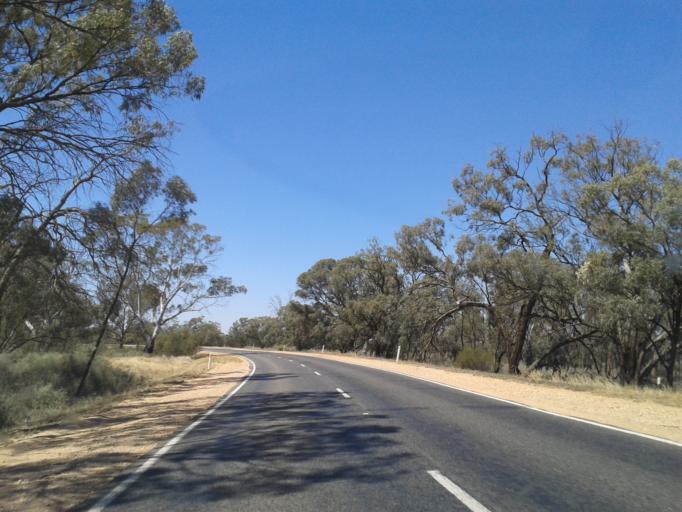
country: AU
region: Victoria
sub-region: Swan Hill
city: Swan Hill
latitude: -34.7205
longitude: 143.1169
